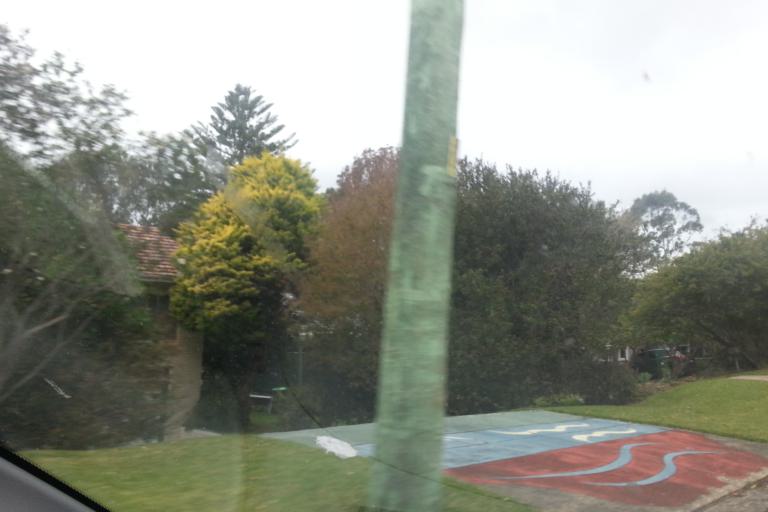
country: AU
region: New South Wales
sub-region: Wollongong
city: Keiraville
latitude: -34.4119
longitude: 150.8672
